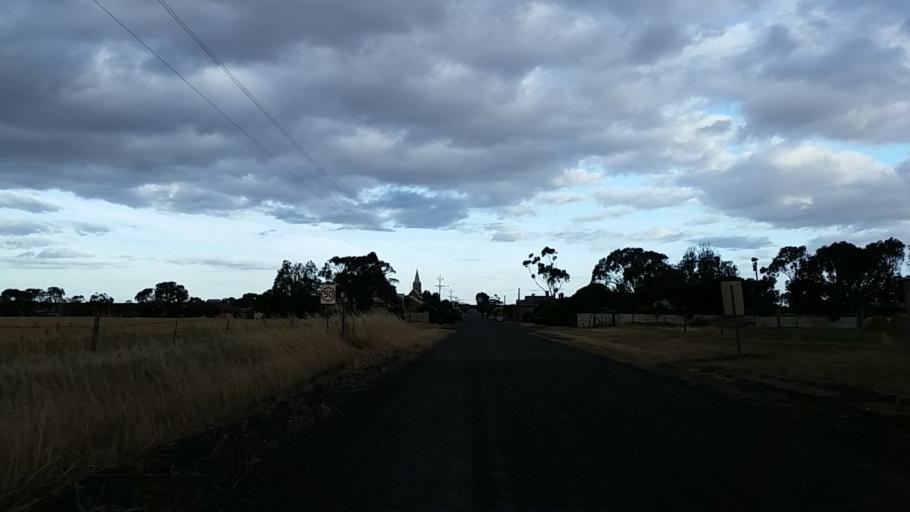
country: AU
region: South Australia
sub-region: Barossa
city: Angaston
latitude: -34.5729
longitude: 139.2908
